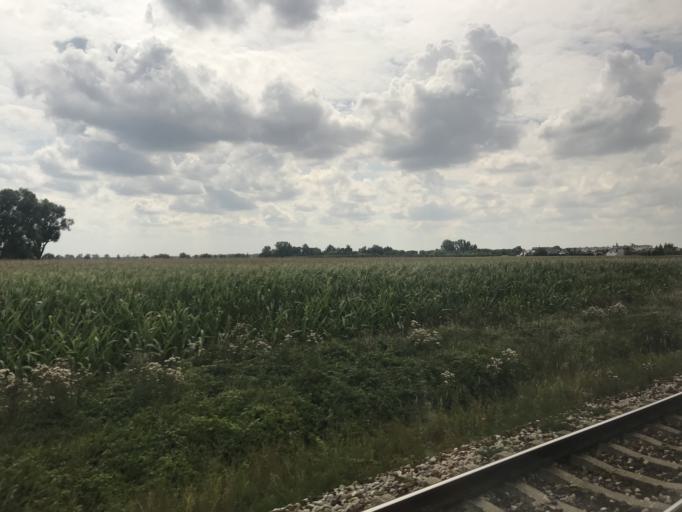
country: PL
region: Greater Poland Voivodeship
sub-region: Powiat poznanski
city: Dopiewo
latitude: 52.3676
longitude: 16.7170
